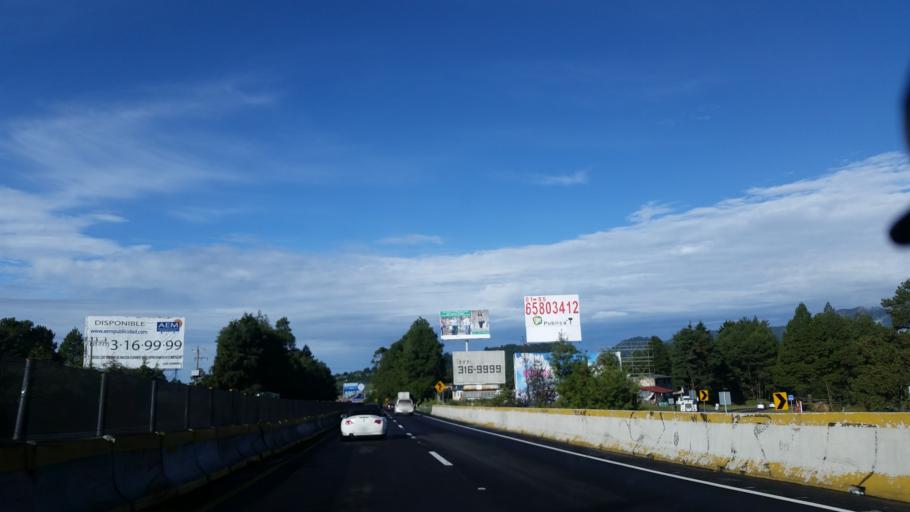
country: MX
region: Morelos
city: Tres Marias
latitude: 19.0719
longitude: -99.2360
